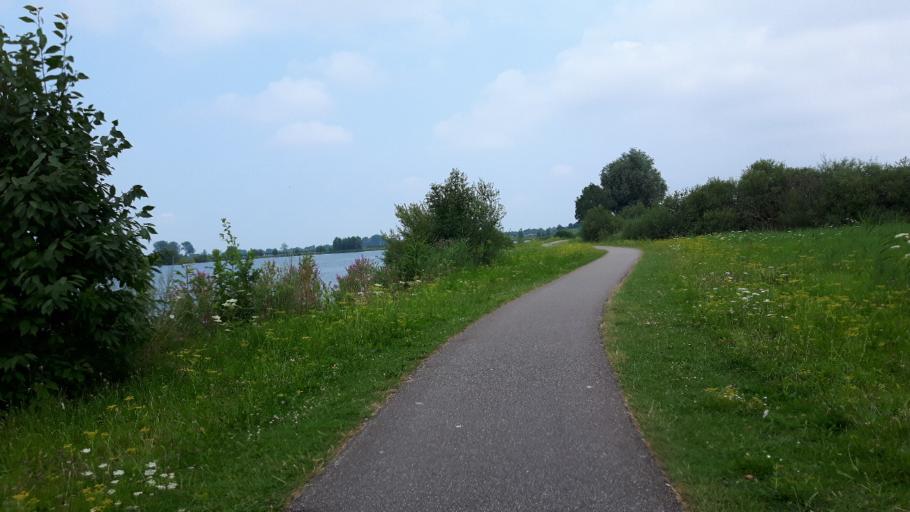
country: NL
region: Utrecht
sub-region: Gemeente IJsselstein
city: IJsselstein
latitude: 52.0312
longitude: 5.0563
